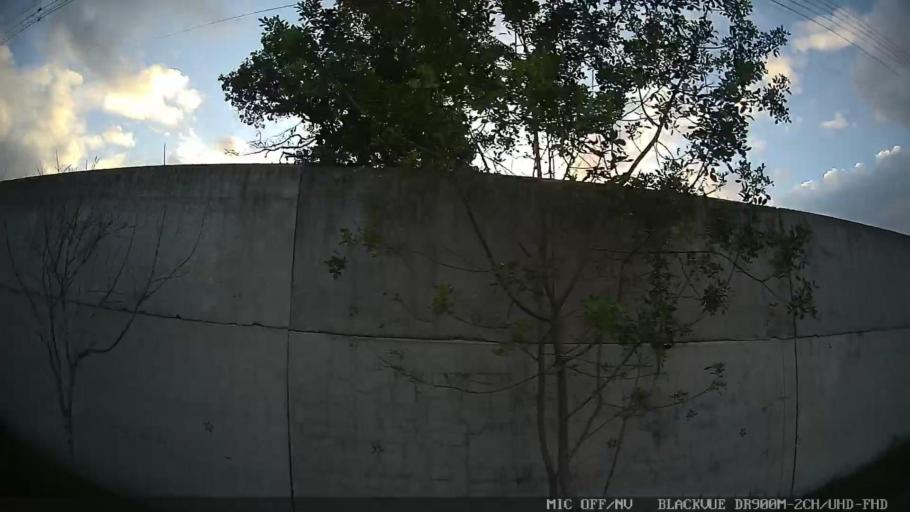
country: BR
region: Sao Paulo
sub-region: Caraguatatuba
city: Caraguatatuba
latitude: -23.6620
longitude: -45.4505
